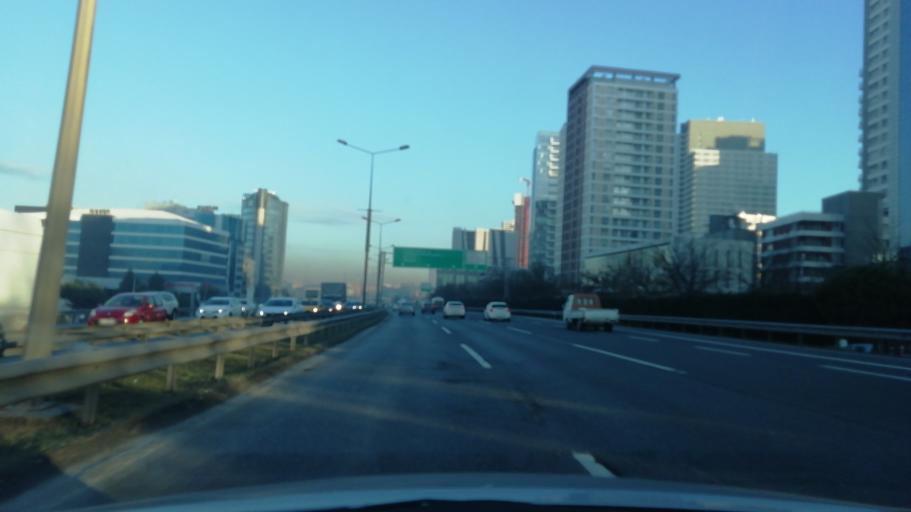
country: TR
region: Istanbul
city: Mahmutbey
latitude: 41.0382
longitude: 28.8106
